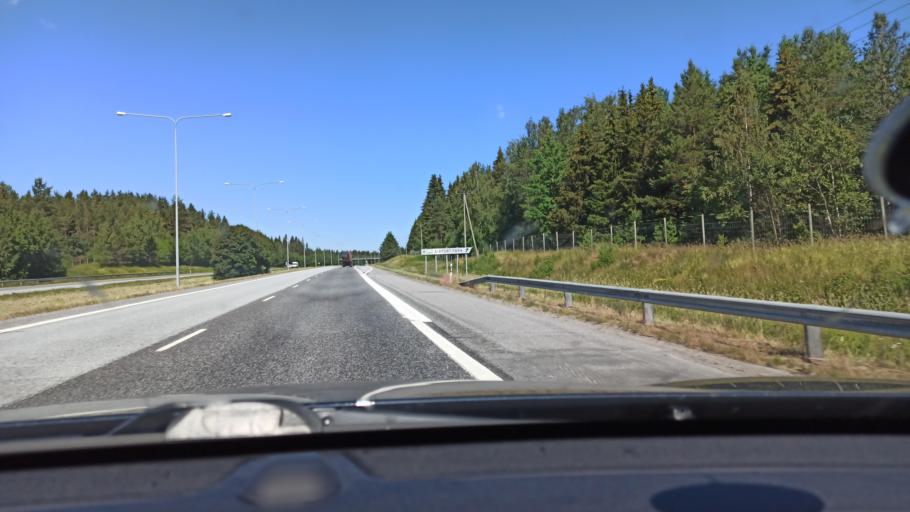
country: FI
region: Ostrobothnia
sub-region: Vaasa
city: Ristinummi
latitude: 63.0486
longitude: 21.7202
